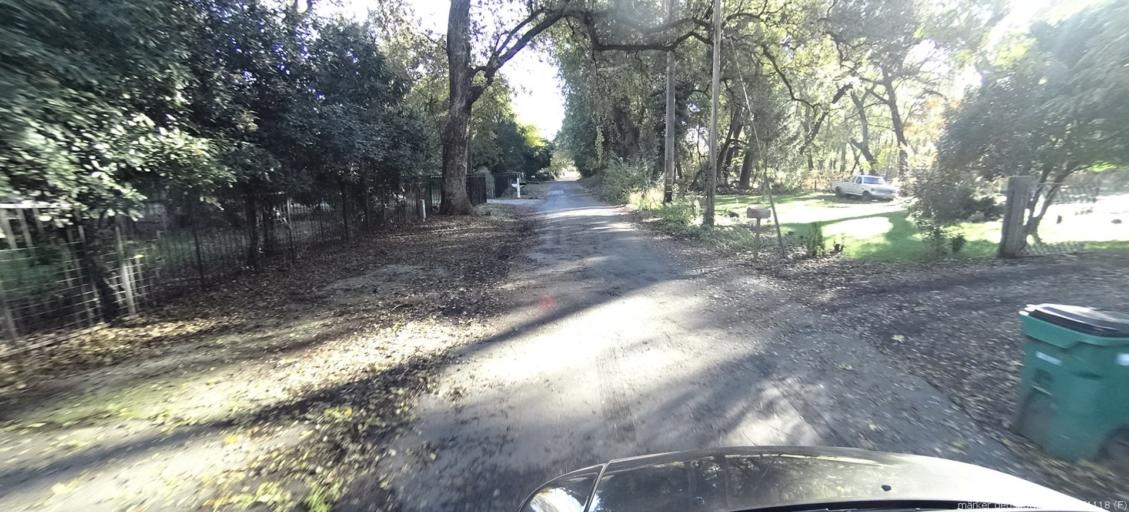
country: US
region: California
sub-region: Shasta County
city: Anderson
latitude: 40.4611
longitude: -122.2386
